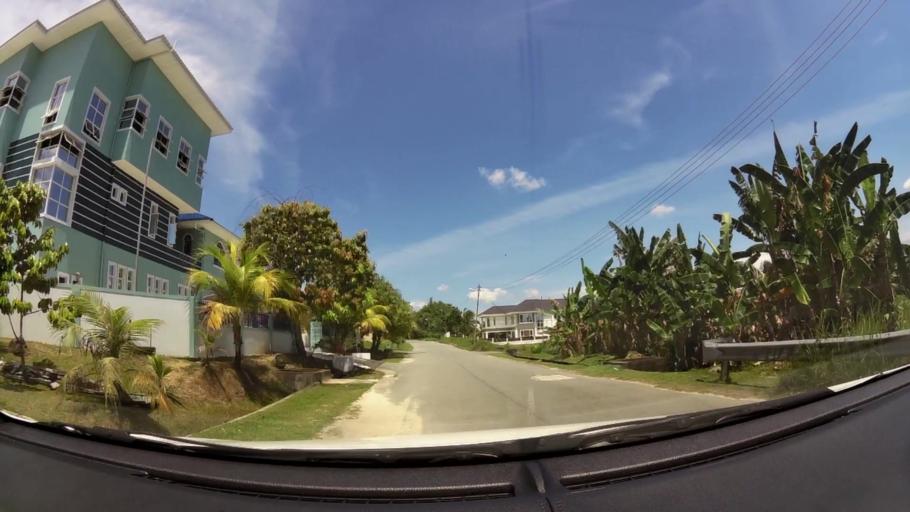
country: BN
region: Brunei and Muara
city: Bandar Seri Begawan
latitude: 4.9433
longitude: 114.9510
